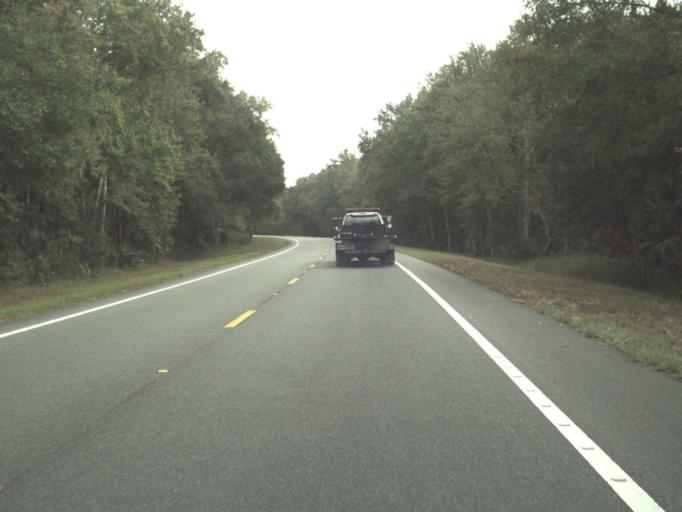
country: US
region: Florida
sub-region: Leon County
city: Woodville
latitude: 30.1590
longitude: -83.9998
